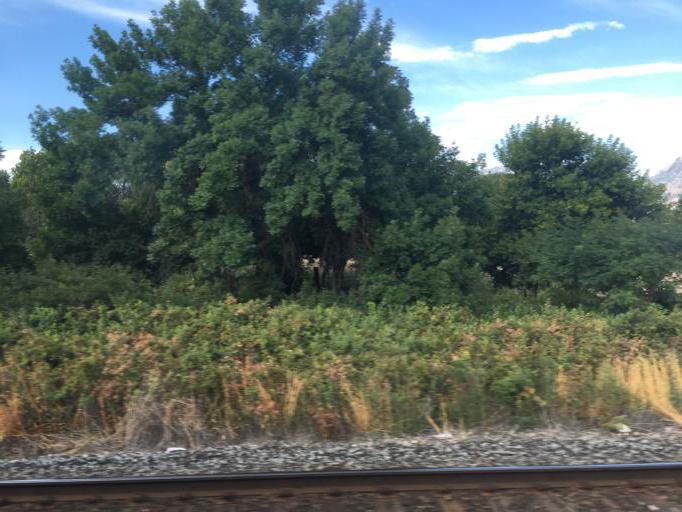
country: US
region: Utah
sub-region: Utah County
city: Lehi
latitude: 40.3819
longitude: -111.8531
